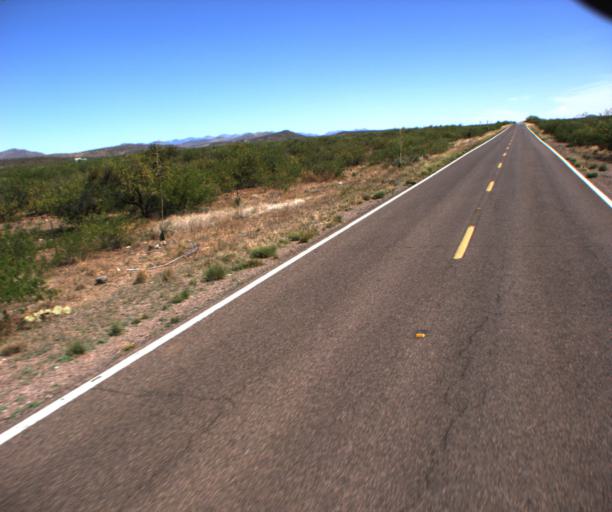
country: US
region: Arizona
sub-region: Cochise County
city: Douglas
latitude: 31.4772
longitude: -109.3525
